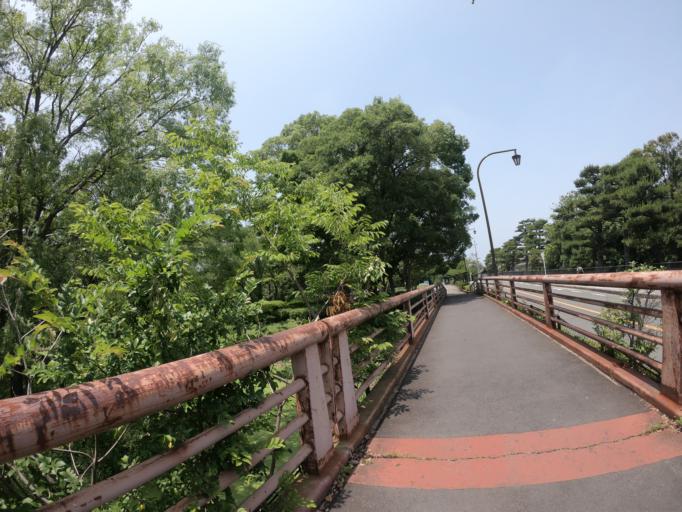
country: JP
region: Osaka
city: Sakai
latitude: 34.5615
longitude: 135.4833
